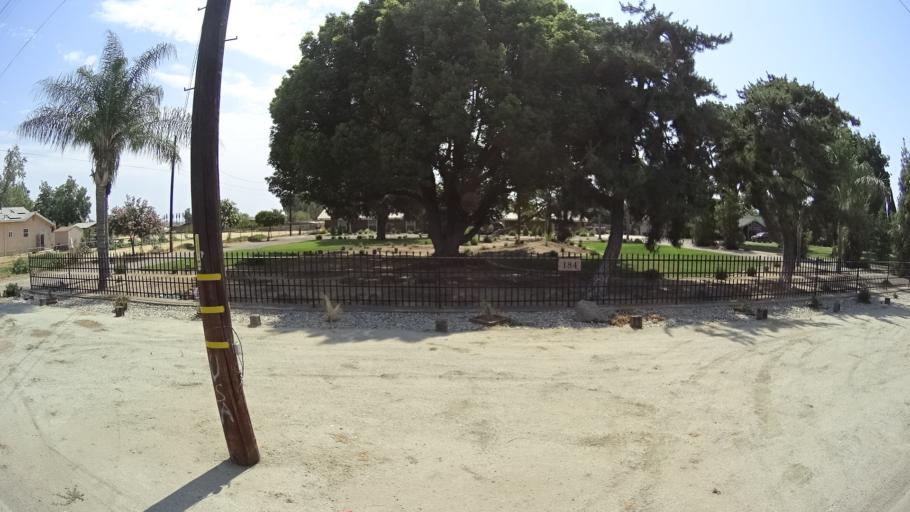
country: US
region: California
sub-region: Fresno County
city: West Park
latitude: 36.7328
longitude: -119.8534
